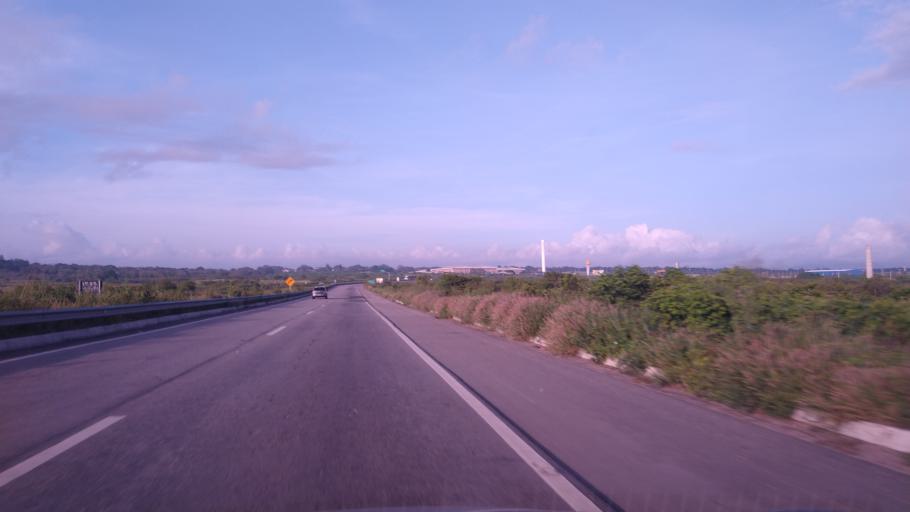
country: BR
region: Ceara
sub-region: Pacajus
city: Pacajus
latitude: -4.1579
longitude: -38.4828
